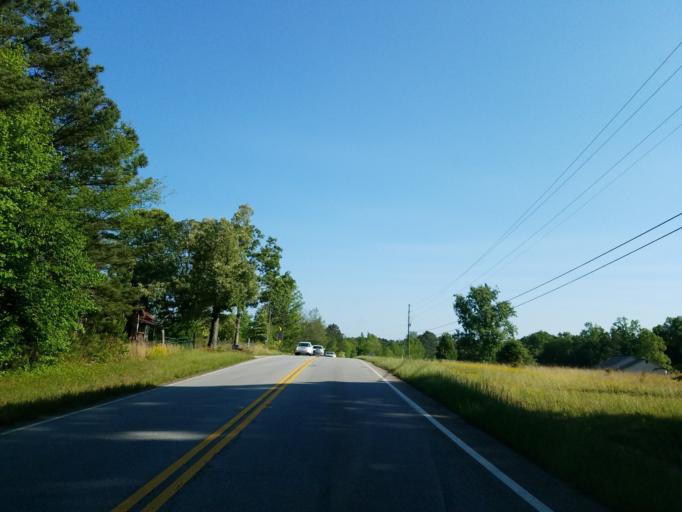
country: US
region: Georgia
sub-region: Carroll County
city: Temple
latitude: 33.8382
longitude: -84.9802
